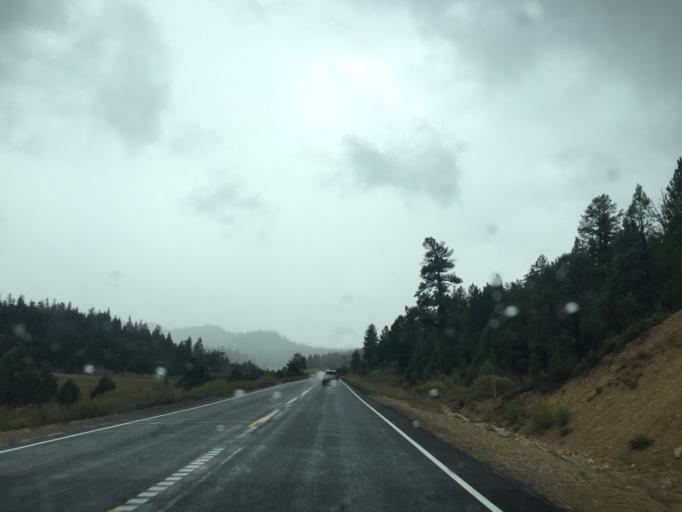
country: US
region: Utah
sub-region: Kane County
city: Kanab
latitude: 37.4363
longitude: -112.5384
